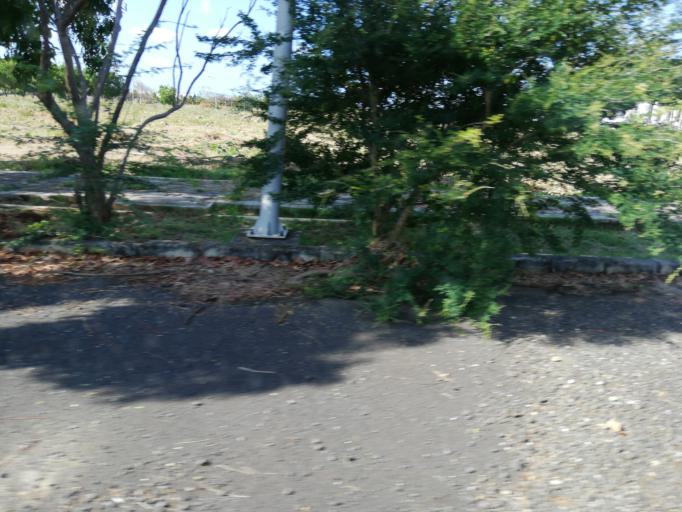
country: MU
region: Port Louis
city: Port Louis
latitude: -20.1593
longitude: 57.4915
